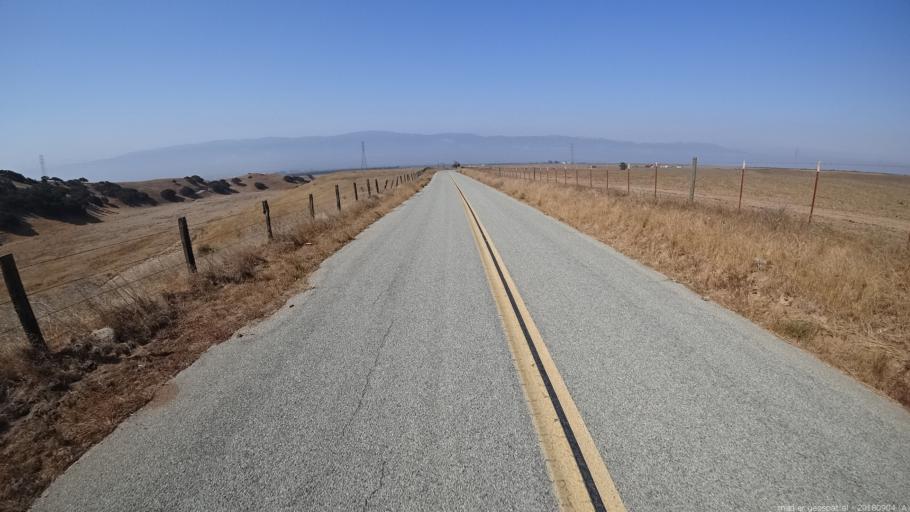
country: US
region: California
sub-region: Monterey County
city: Soledad
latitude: 36.5116
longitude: -121.3530
